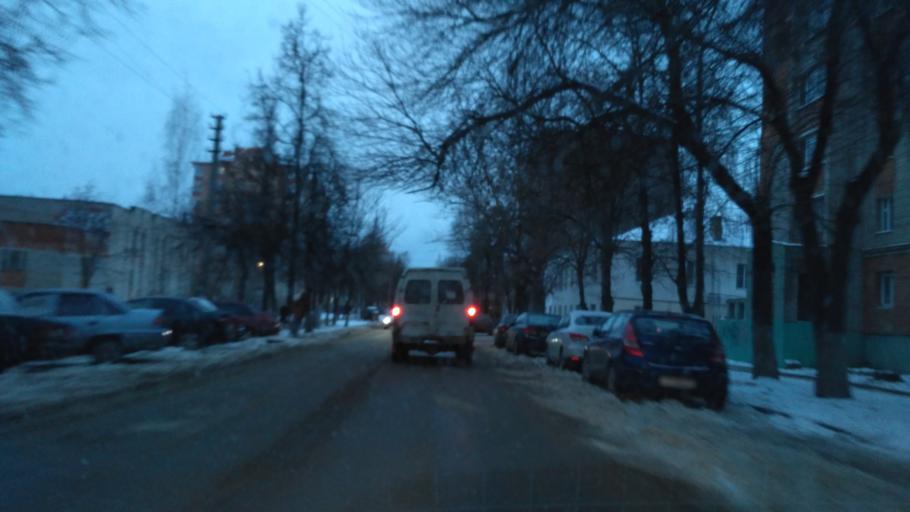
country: RU
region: Tula
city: Mendeleyevskiy
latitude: 54.1681
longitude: 37.5818
